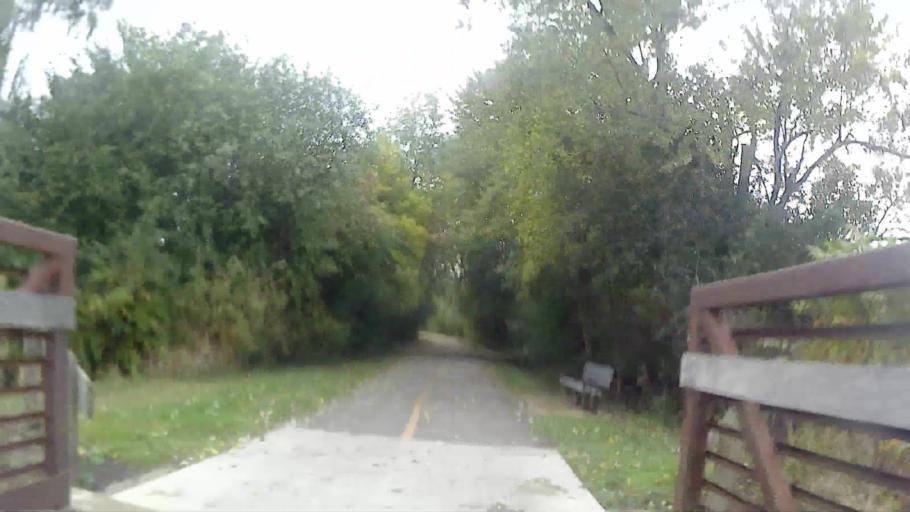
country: US
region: Illinois
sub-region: Kane County
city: Montgomery
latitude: 41.7560
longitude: -88.3822
